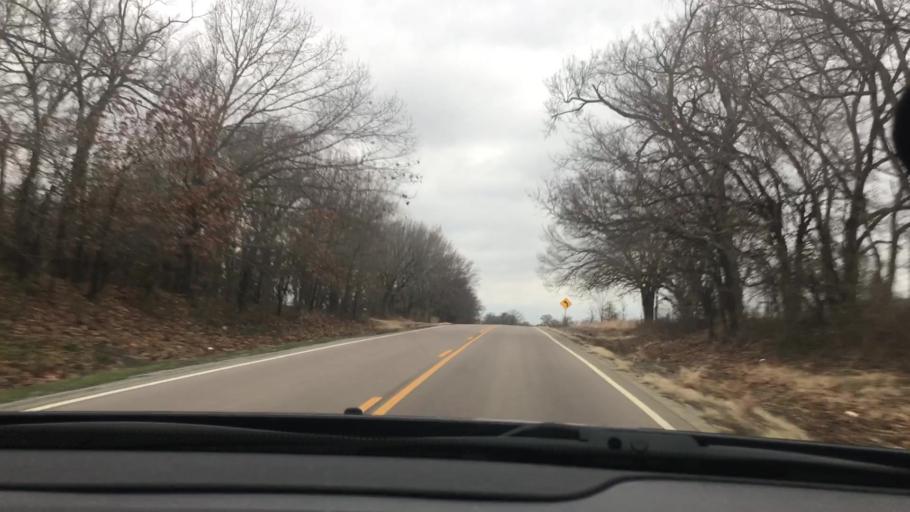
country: US
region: Oklahoma
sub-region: Coal County
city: Coalgate
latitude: 34.3728
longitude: -96.3571
